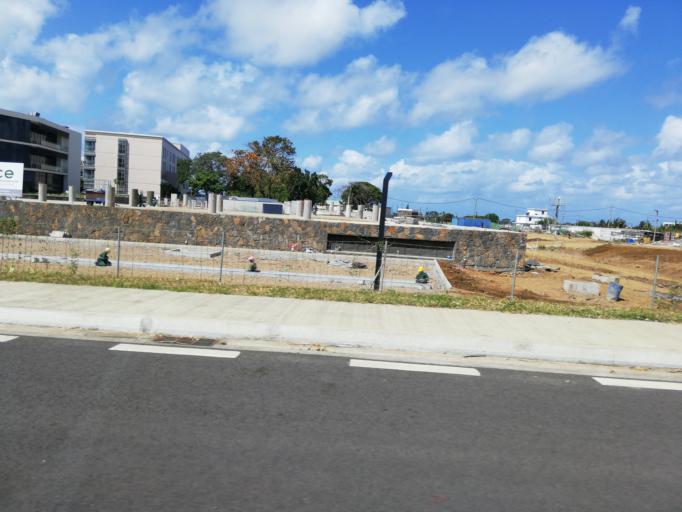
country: MU
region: Grand Port
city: Plaine Magnien
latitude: -20.4402
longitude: 57.6698
